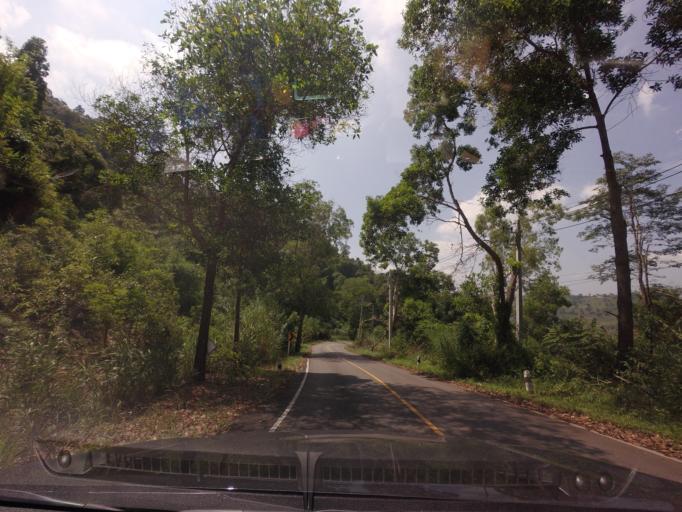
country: TH
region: Loei
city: Na Haeo
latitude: 17.4933
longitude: 100.8945
